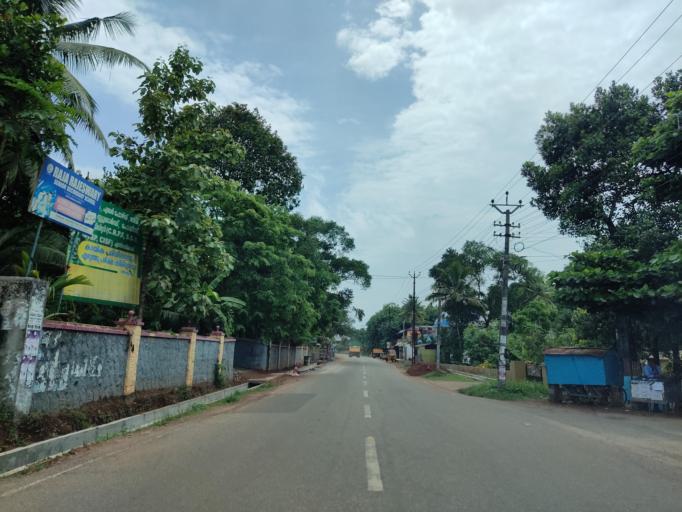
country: IN
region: Kerala
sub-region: Alappuzha
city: Mavelikara
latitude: 9.2266
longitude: 76.6148
